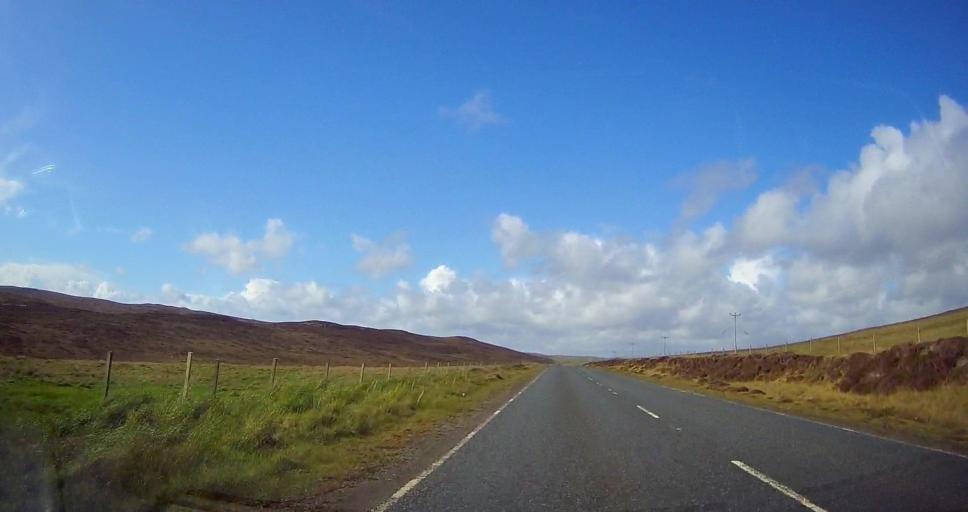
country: GB
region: Scotland
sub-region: Shetland Islands
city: Lerwick
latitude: 60.2023
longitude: -1.2332
